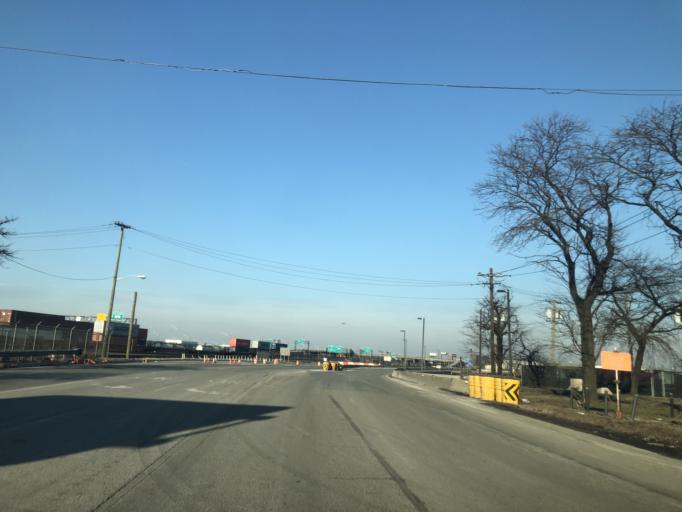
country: US
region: New Jersey
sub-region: Essex County
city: Newark
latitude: 40.6974
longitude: -74.1547
